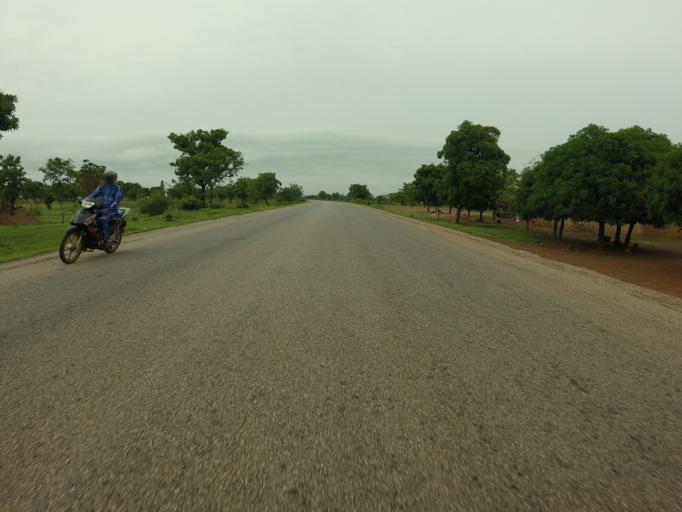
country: GH
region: Northern
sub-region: Yendi
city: Yendi
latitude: 9.5175
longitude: -0.0289
